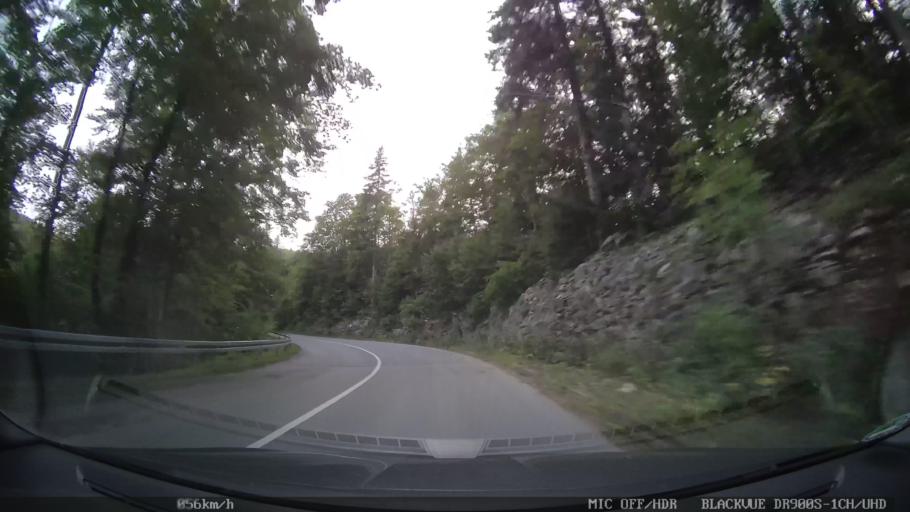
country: HR
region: Primorsko-Goranska
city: Novi Vinodolski
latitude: 45.1744
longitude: 14.9749
